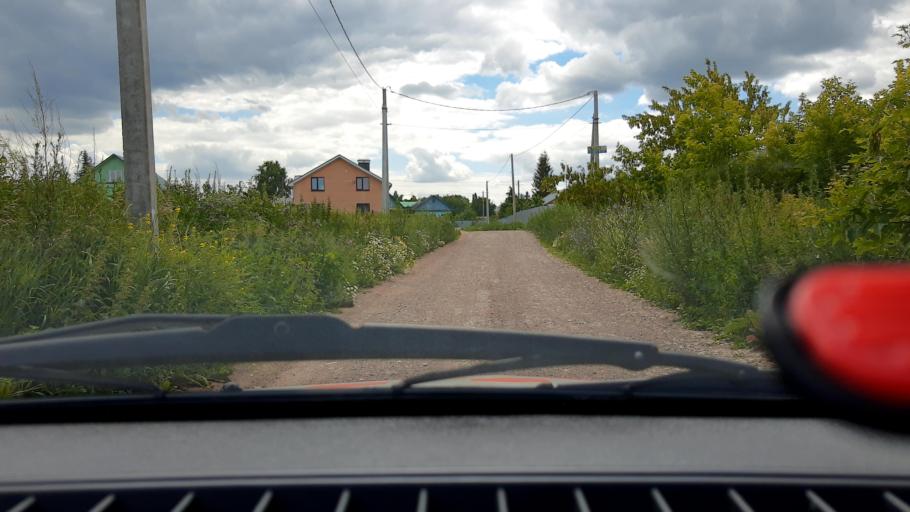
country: RU
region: Bashkortostan
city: Avdon
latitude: 54.5016
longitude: 55.8967
